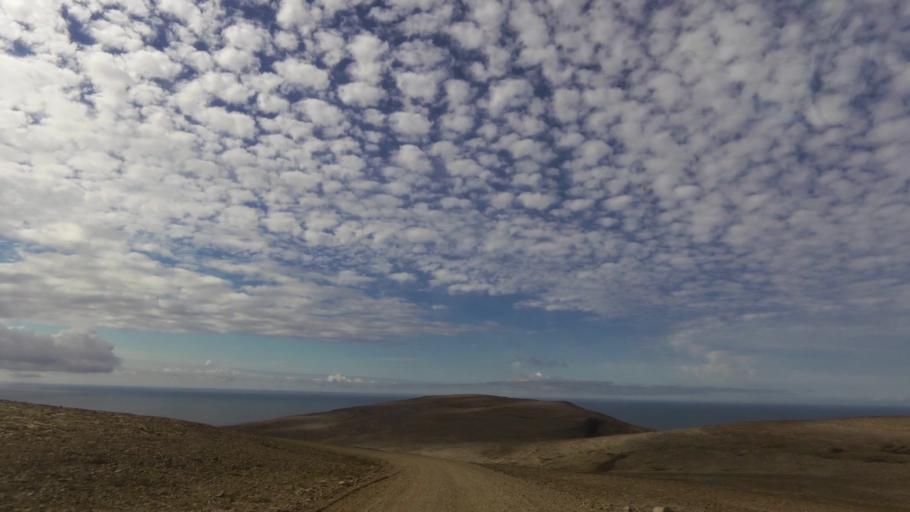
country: IS
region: West
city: Olafsvik
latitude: 65.6226
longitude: -24.2815
